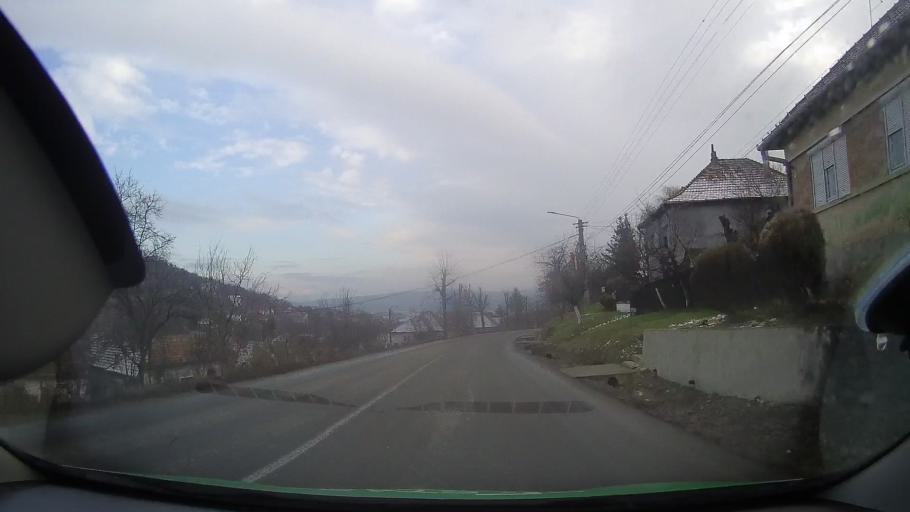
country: RO
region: Mures
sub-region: Municipiul Tarnaveni
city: Tarnaveni
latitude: 46.3378
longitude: 24.2850
